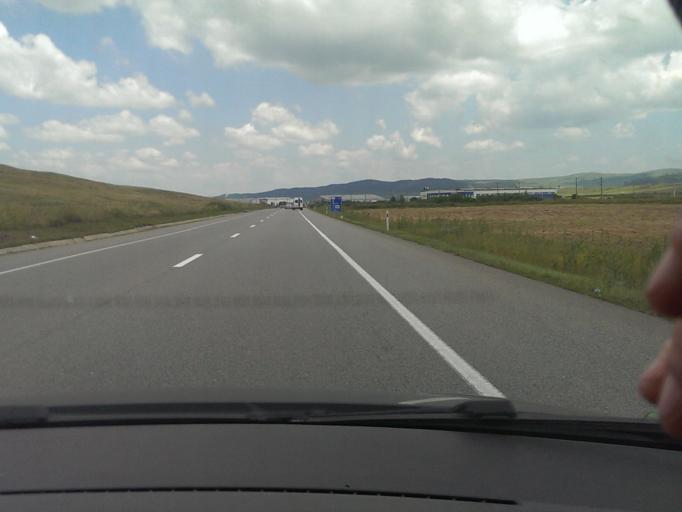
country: RO
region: Cluj
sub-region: Comuna Bontida
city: Rascruci
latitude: 46.8857
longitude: 23.7770
